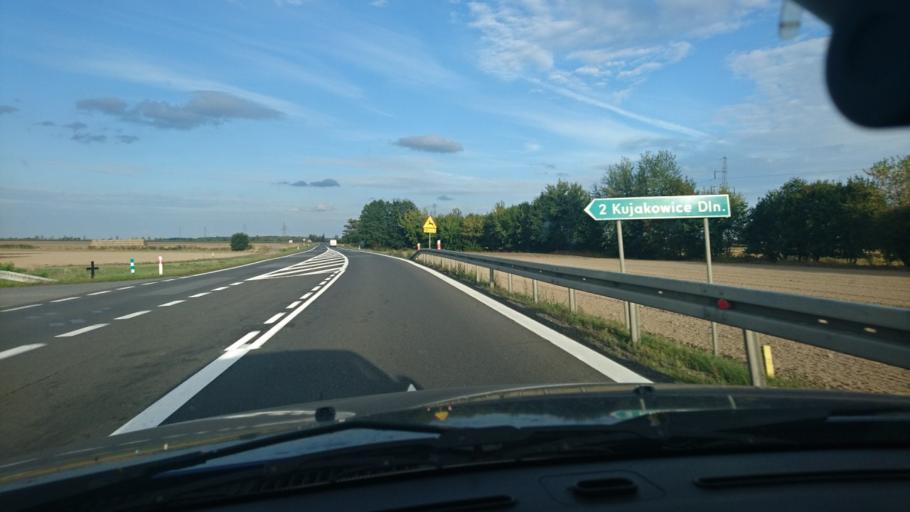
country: PL
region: Opole Voivodeship
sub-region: Powiat kluczborski
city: Kluczbork
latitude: 50.9913
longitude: 18.2155
